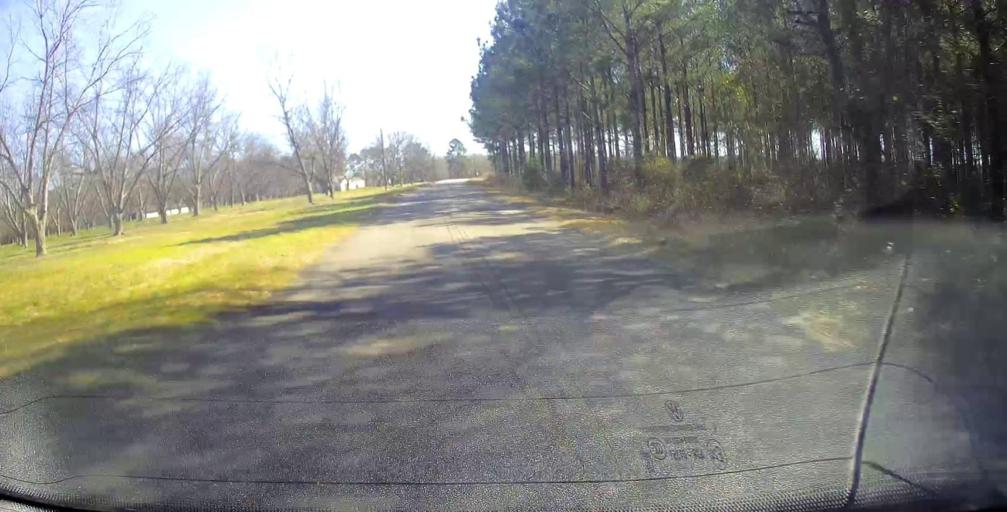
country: US
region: Georgia
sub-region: Peach County
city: Fort Valley
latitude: 32.6349
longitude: -83.8555
